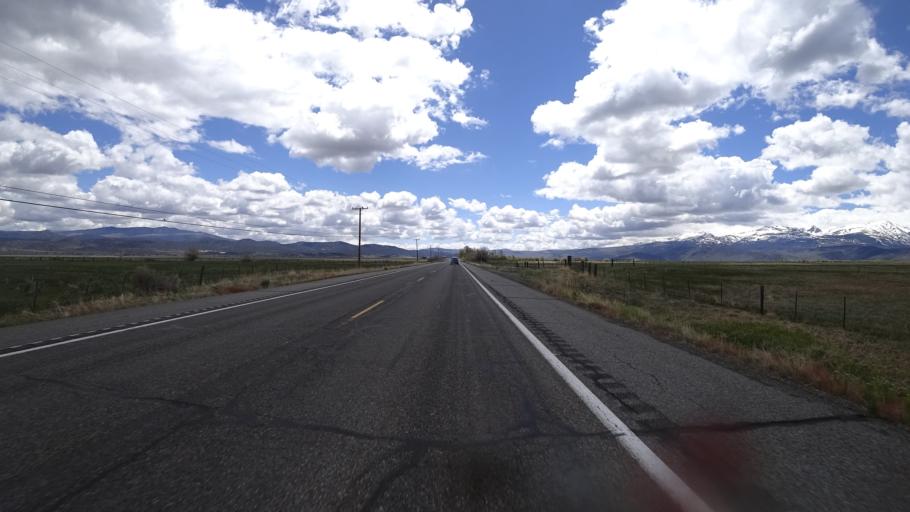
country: US
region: California
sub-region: Mono County
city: Bridgeport
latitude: 38.2617
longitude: -119.2754
